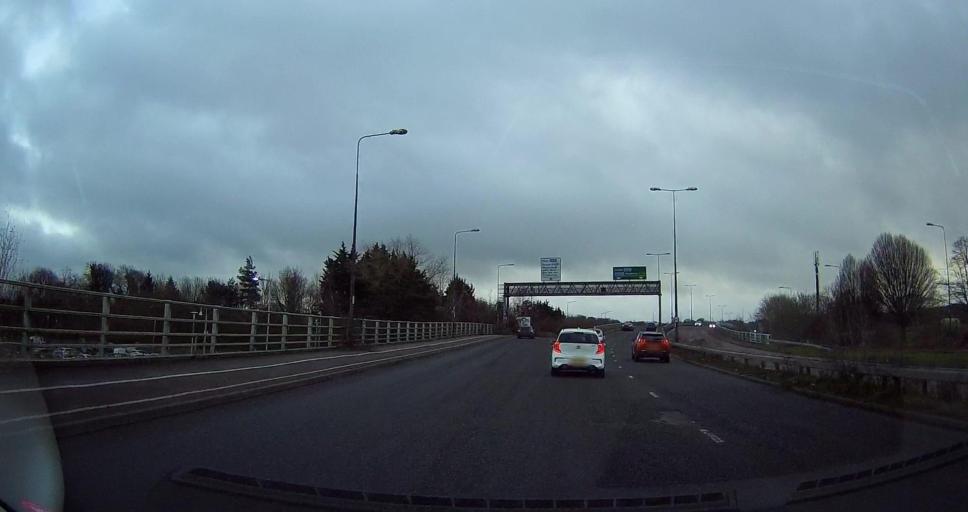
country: GB
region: England
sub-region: Kent
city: Chatham
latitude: 51.3446
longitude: 0.5074
